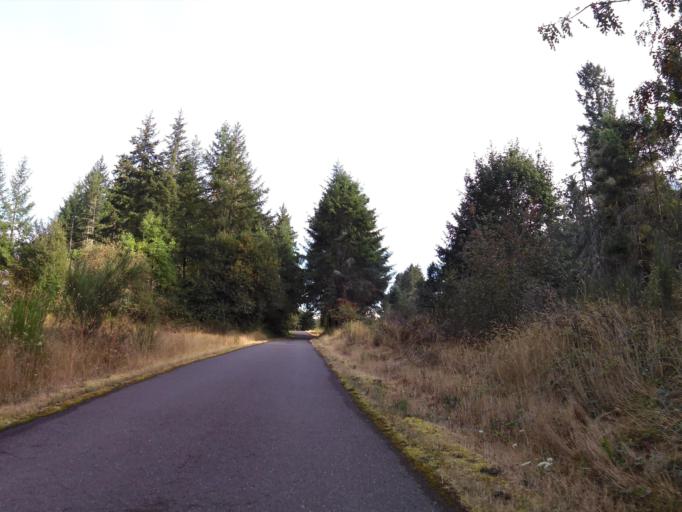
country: US
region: Washington
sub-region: Thurston County
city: Tenino
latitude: 46.9181
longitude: -122.8002
